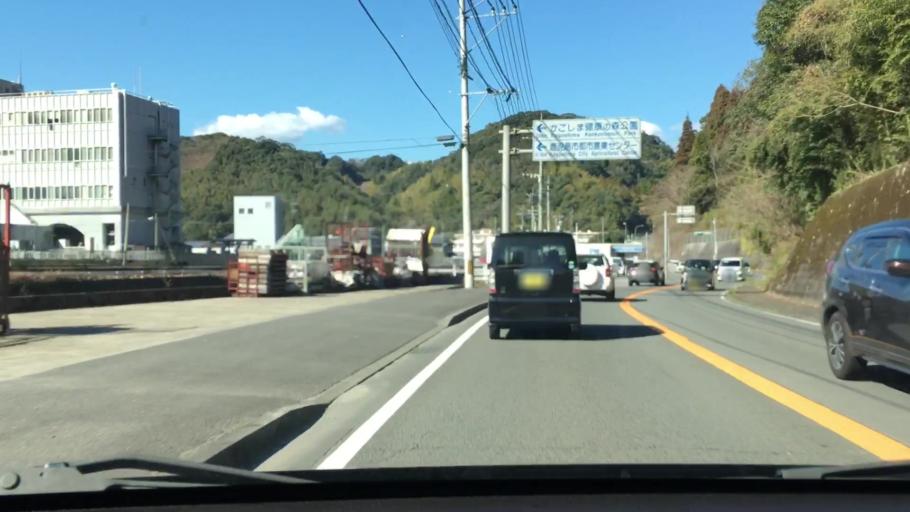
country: JP
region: Kagoshima
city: Kagoshima-shi
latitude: 31.6405
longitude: 130.5160
